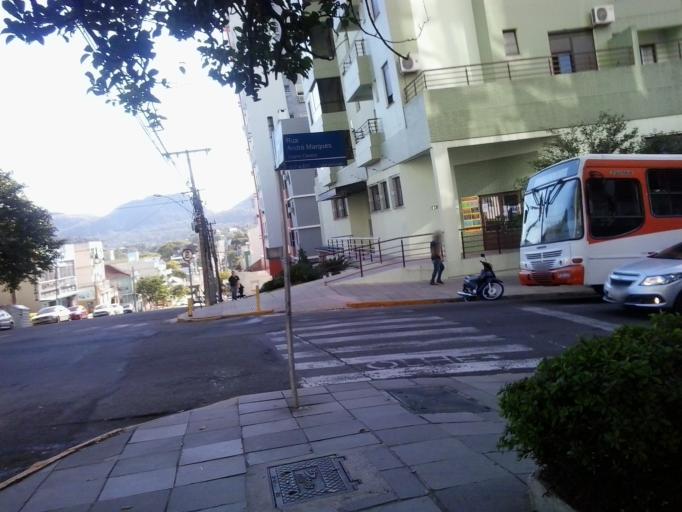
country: BR
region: Rio Grande do Sul
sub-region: Santa Maria
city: Santa Maria
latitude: -29.6826
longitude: -53.8057
